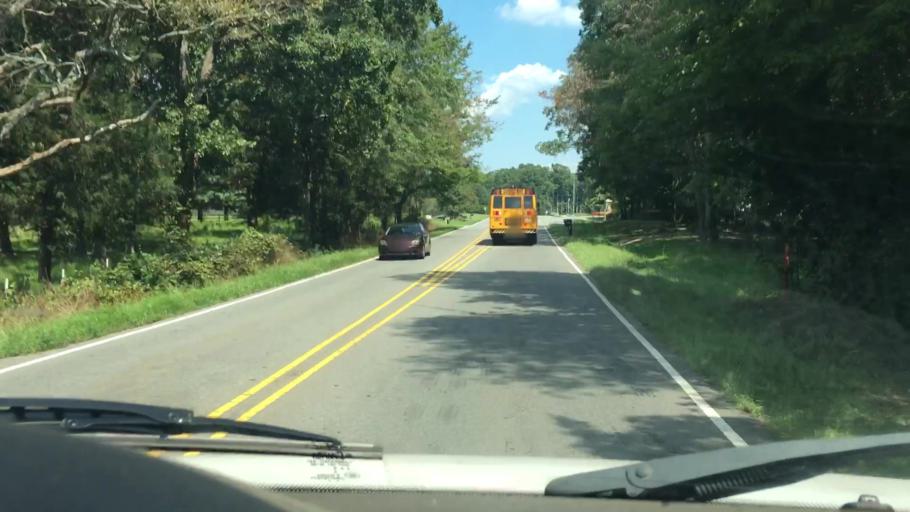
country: US
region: North Carolina
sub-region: Mecklenburg County
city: Huntersville
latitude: 35.3638
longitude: -80.8612
